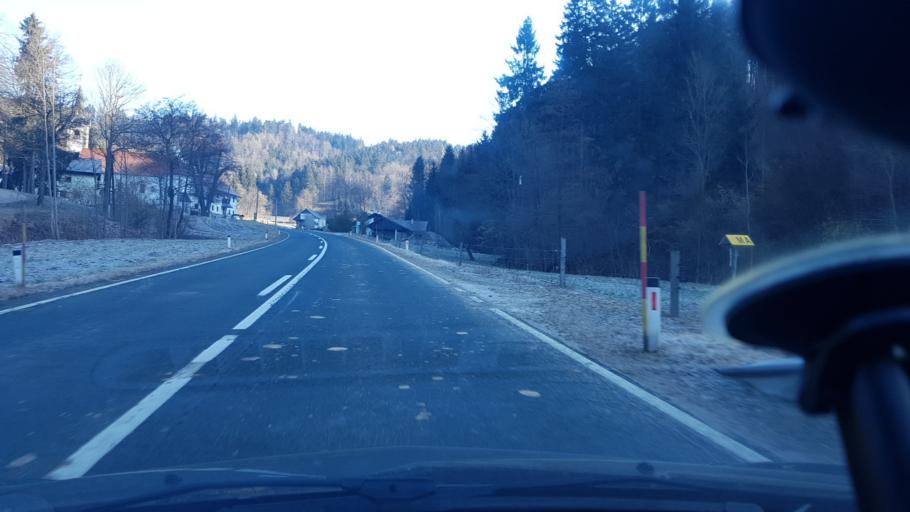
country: SI
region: Zagorje ob Savi
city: Izlake
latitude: 46.1842
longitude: 14.8597
